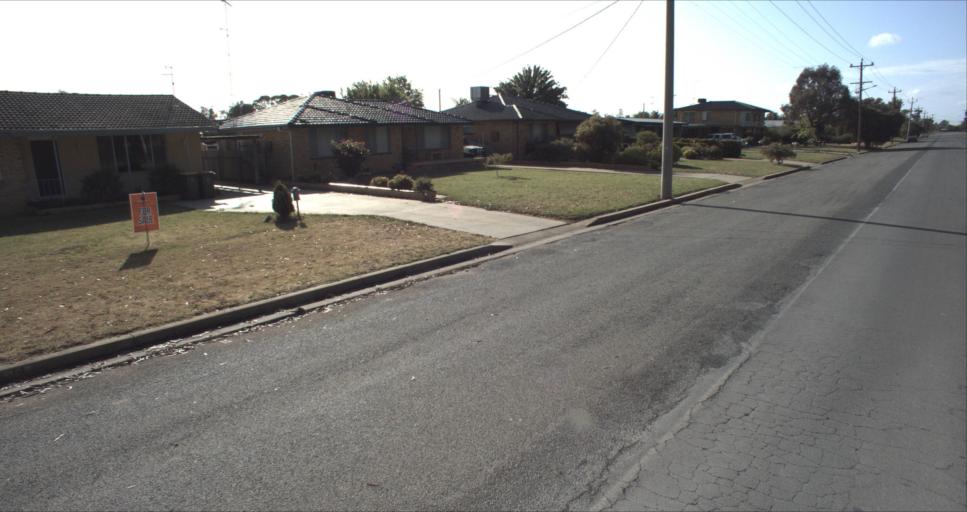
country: AU
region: New South Wales
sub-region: Leeton
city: Leeton
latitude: -34.5552
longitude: 146.3882
